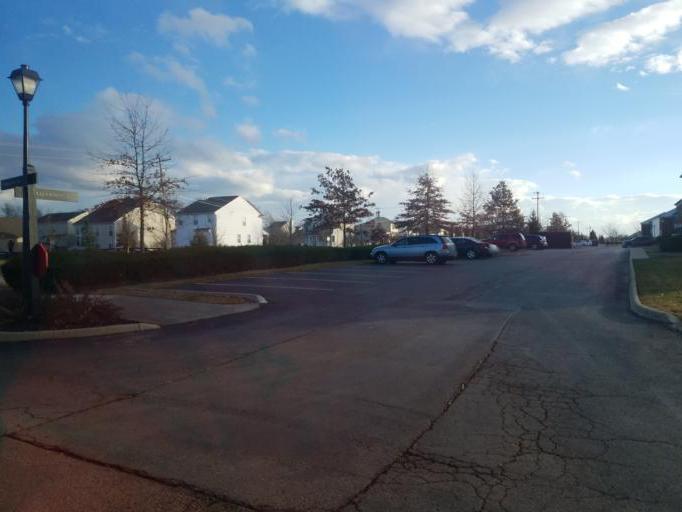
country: US
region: Ohio
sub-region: Delaware County
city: Delaware
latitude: 40.3188
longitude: -83.1089
